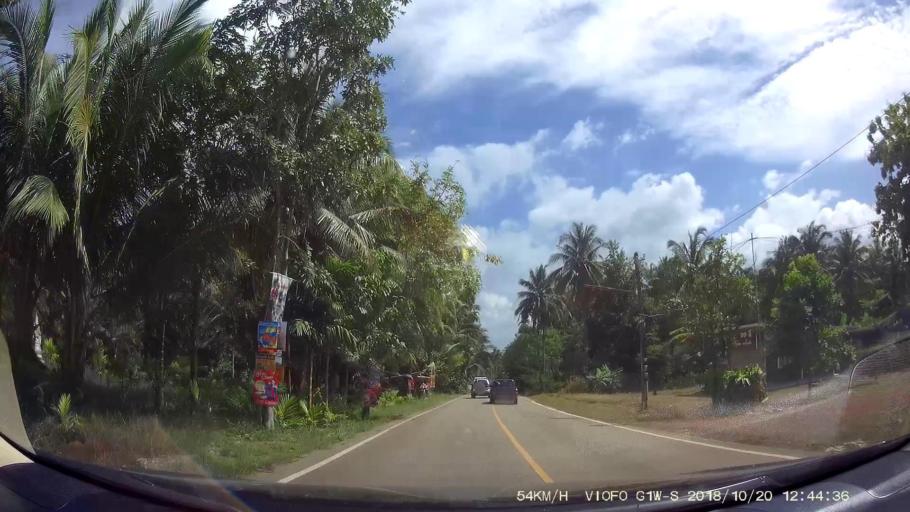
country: TH
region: Chaiyaphum
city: Khon San
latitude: 16.5384
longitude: 101.8702
